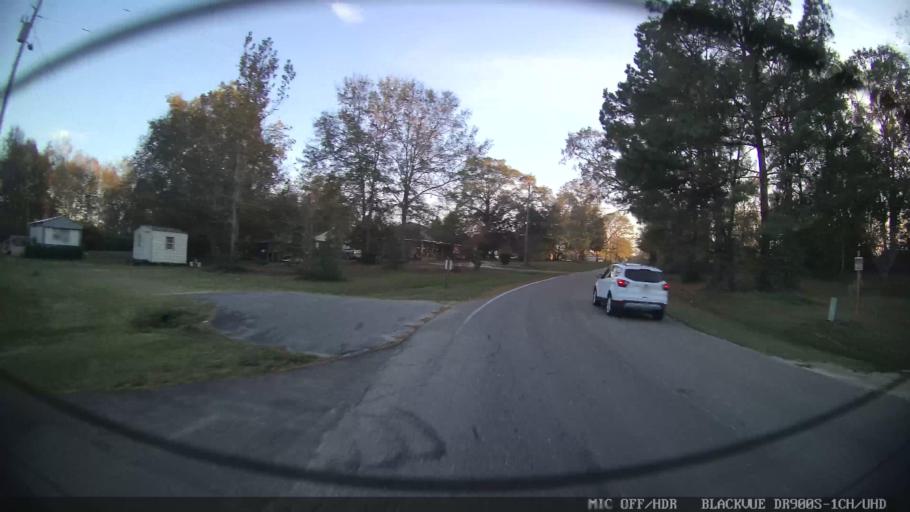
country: US
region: Mississippi
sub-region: Stone County
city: Wiggins
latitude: 30.9952
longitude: -89.2588
